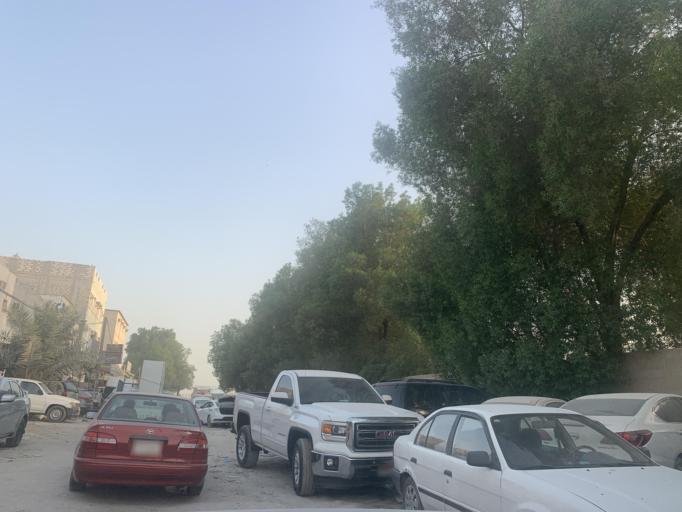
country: BH
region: Central Governorate
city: Madinat Hamad
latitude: 26.1378
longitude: 50.4839
